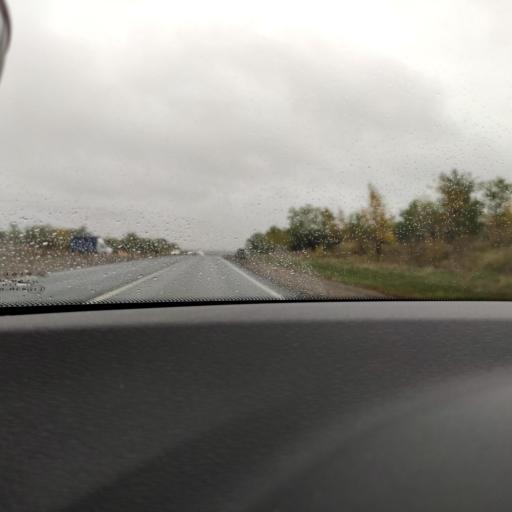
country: RU
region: Samara
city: Mirnyy
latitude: 53.6399
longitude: 50.2287
